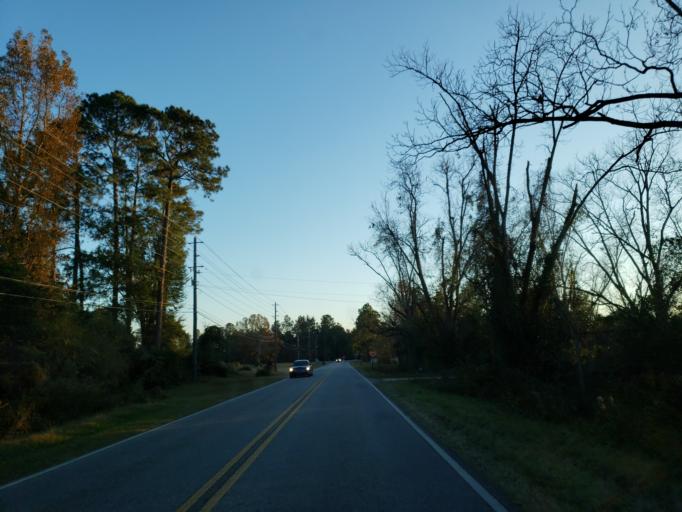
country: US
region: Georgia
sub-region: Crisp County
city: Cordele
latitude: 31.9292
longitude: -83.7663
